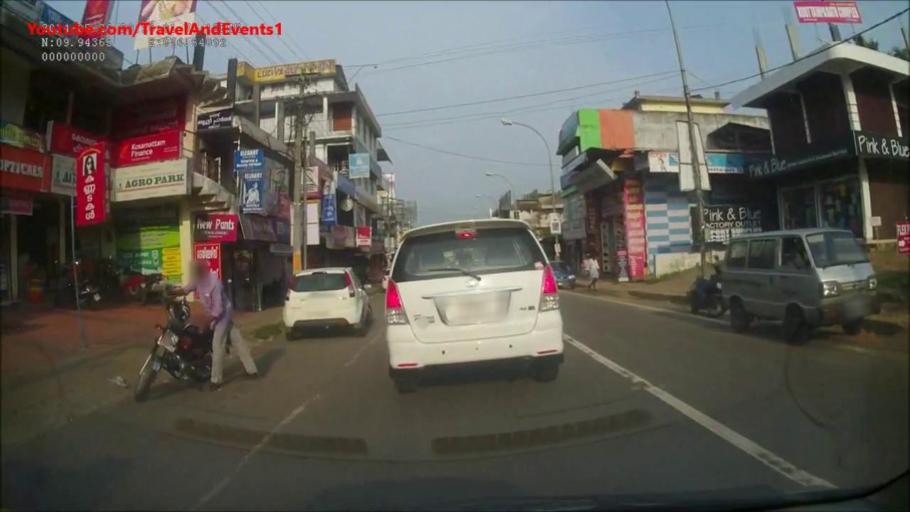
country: IN
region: Kerala
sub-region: Ernakulam
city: Muvattupula
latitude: 9.9393
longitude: 76.6483
